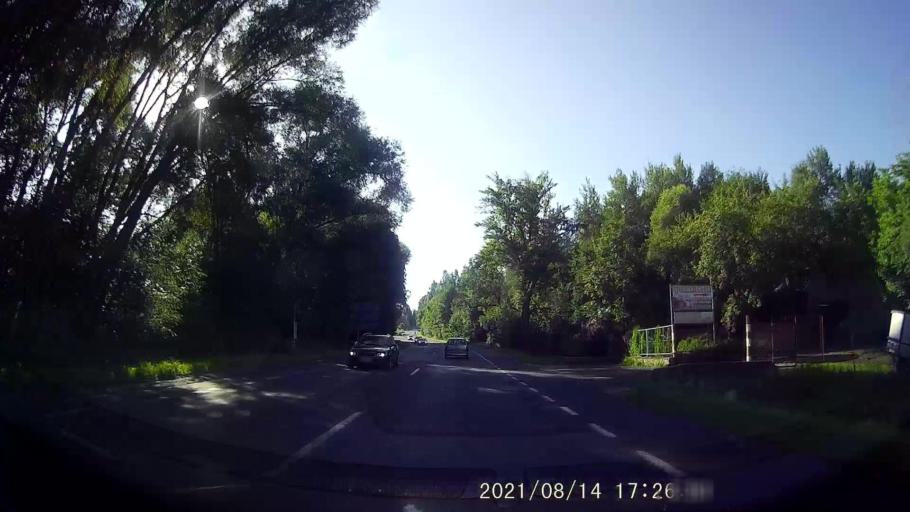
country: PL
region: Lower Silesian Voivodeship
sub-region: Jelenia Gora
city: Jelenia Gora
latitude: 50.9068
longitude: 15.7129
